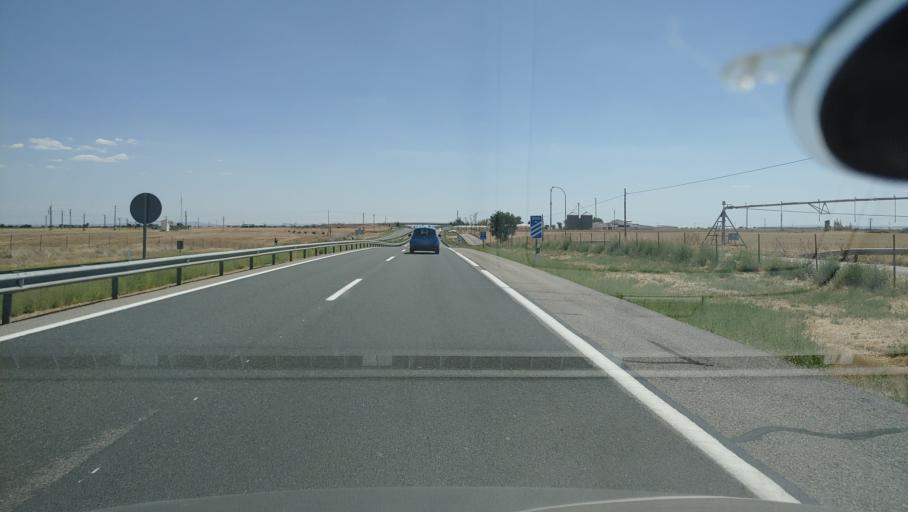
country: ES
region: Castille-La Mancha
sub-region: Provincia de Ciudad Real
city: Villarta de San Juan
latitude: 39.1757
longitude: -3.3964
